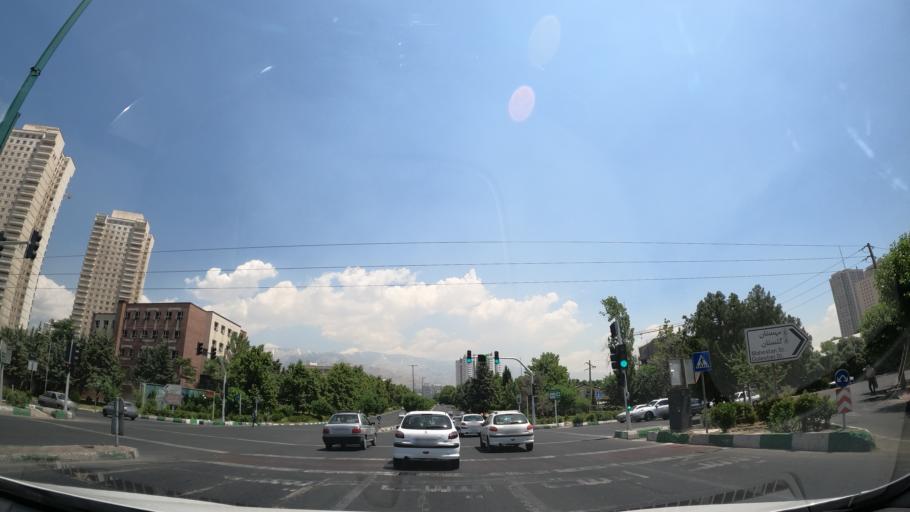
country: IR
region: Tehran
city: Tajrish
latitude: 35.7616
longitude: 51.3757
